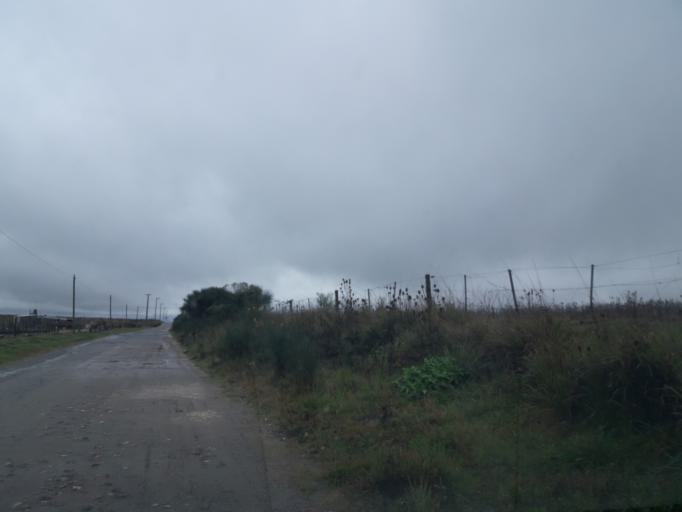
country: AR
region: Buenos Aires
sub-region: Partido de Tandil
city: Tandil
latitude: -37.3282
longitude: -59.1812
